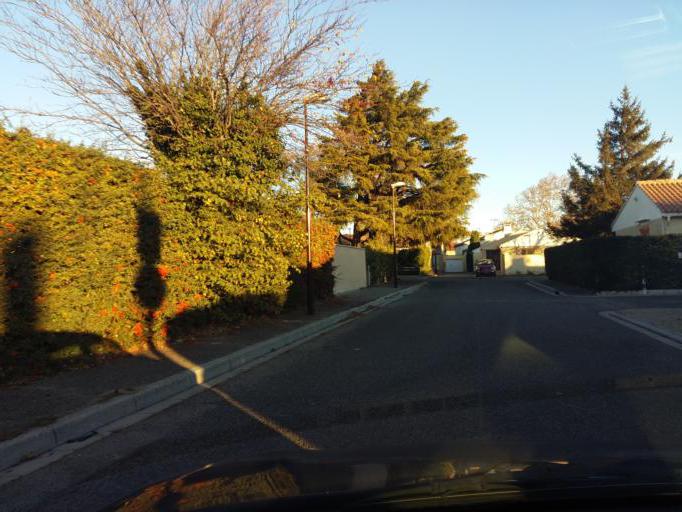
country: FR
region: Provence-Alpes-Cote d'Azur
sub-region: Departement du Vaucluse
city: Montfavet
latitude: 43.9332
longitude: 4.8409
